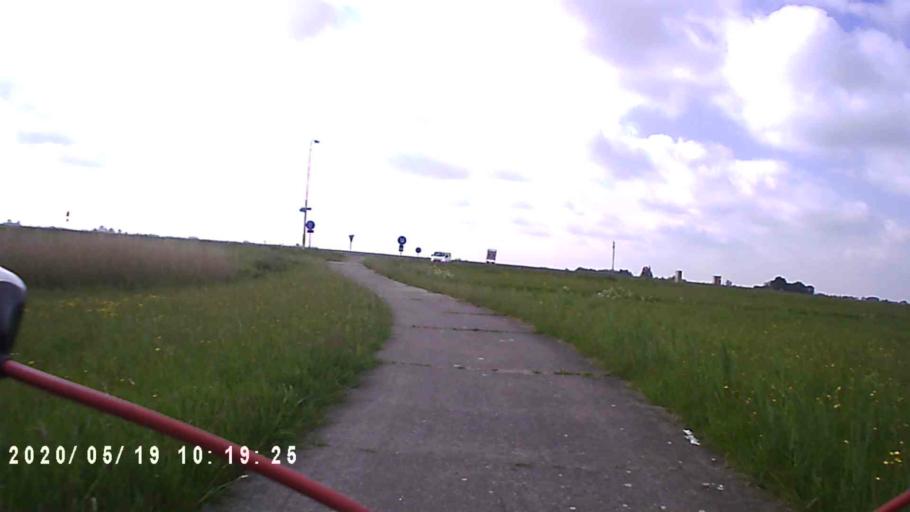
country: NL
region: Friesland
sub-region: Gemeente Kollumerland en Nieuwkruisland
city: Kollum
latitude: 53.3207
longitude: 6.2056
